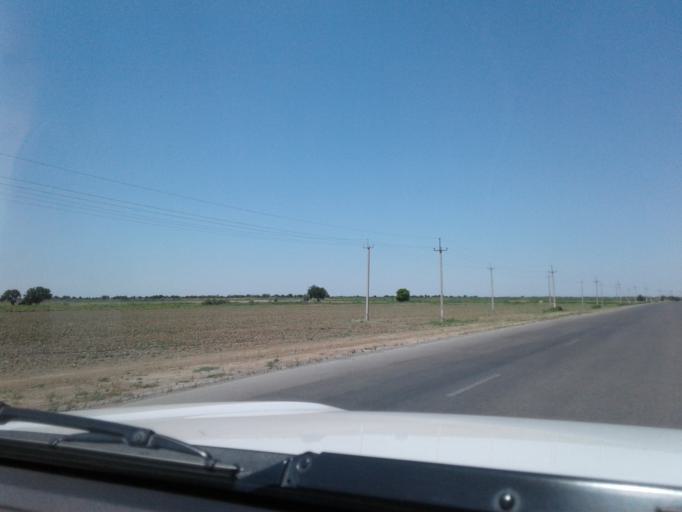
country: TM
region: Mary
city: Bayramaly
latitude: 37.6062
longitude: 62.2461
